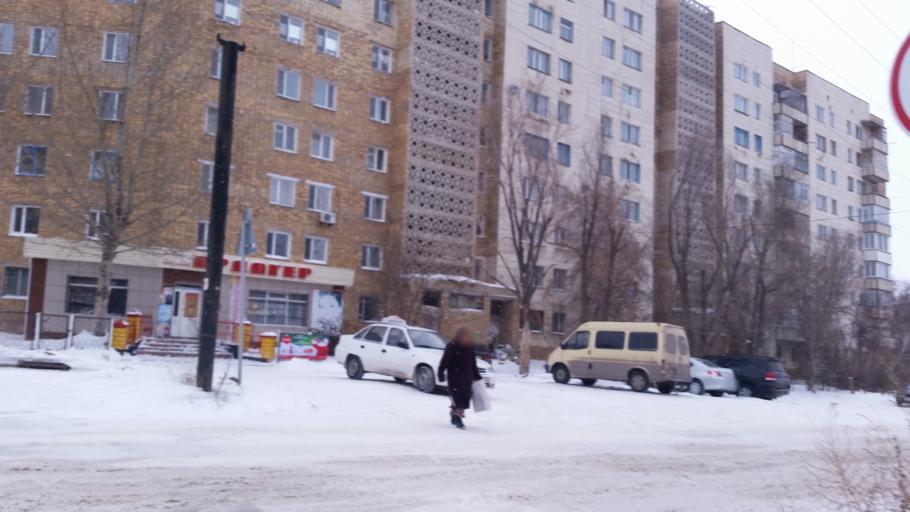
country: KZ
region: Qaraghandy
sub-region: Qaraghandy Qalasy
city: Karagandy
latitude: 49.7734
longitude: 73.1544
